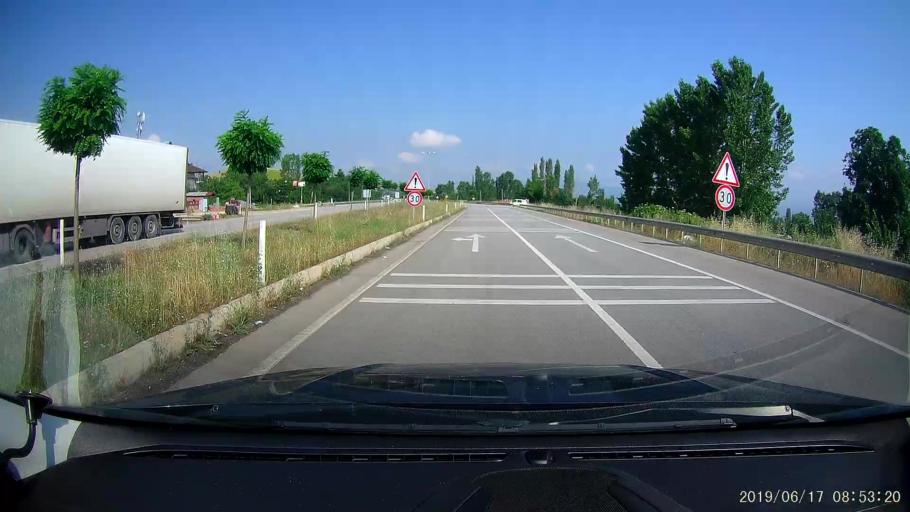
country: TR
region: Tokat
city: Erbaa
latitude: 40.7090
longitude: 36.4830
